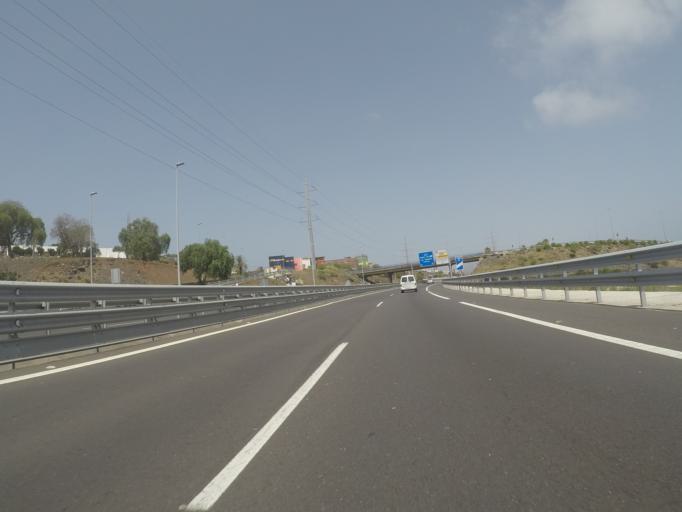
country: ES
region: Canary Islands
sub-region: Provincia de Santa Cruz de Tenerife
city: Santa Cruz de Tenerife
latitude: 28.4434
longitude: -16.2778
